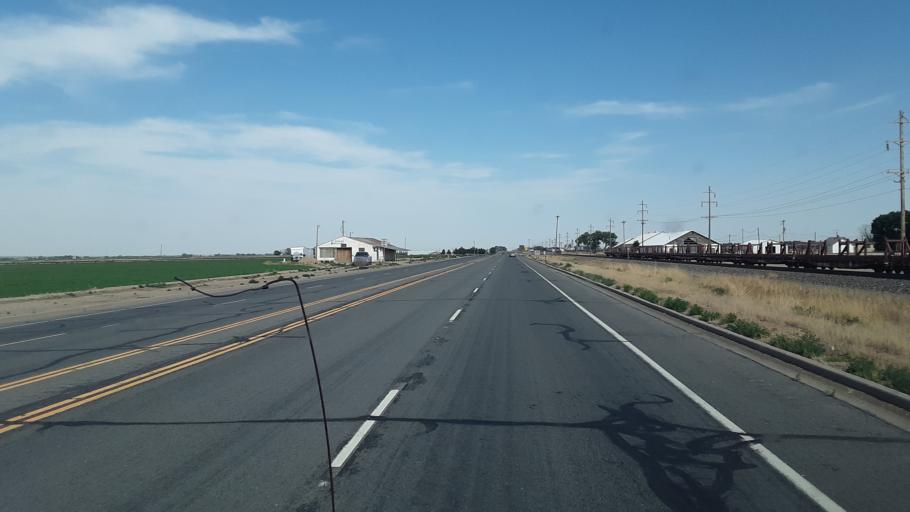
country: US
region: Colorado
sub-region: Otero County
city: Rocky Ford
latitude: 38.0884
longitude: -103.8077
